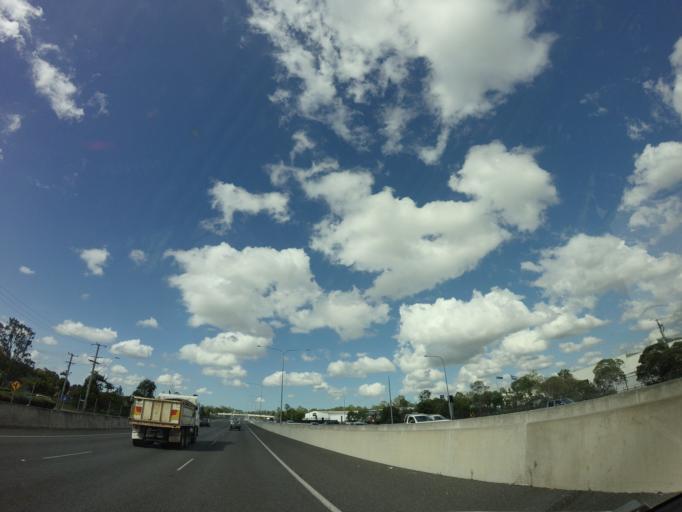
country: AU
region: Queensland
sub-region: Brisbane
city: Wacol
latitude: -27.5921
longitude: 152.9244
